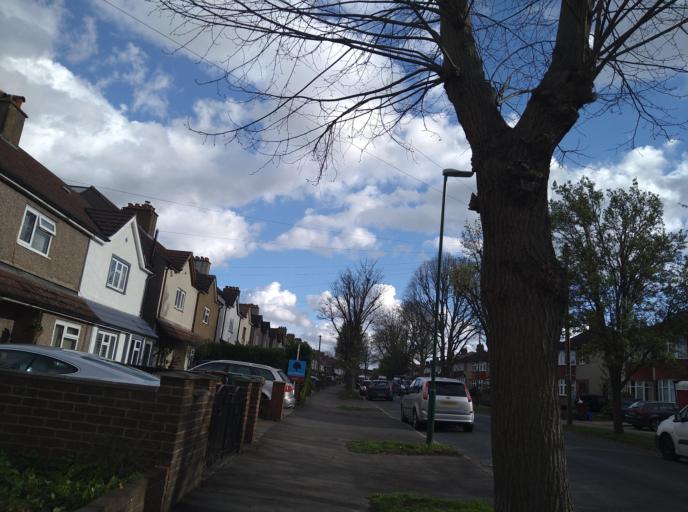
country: GB
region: England
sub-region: Greater London
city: Carshalton
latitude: 51.3719
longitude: -0.1841
